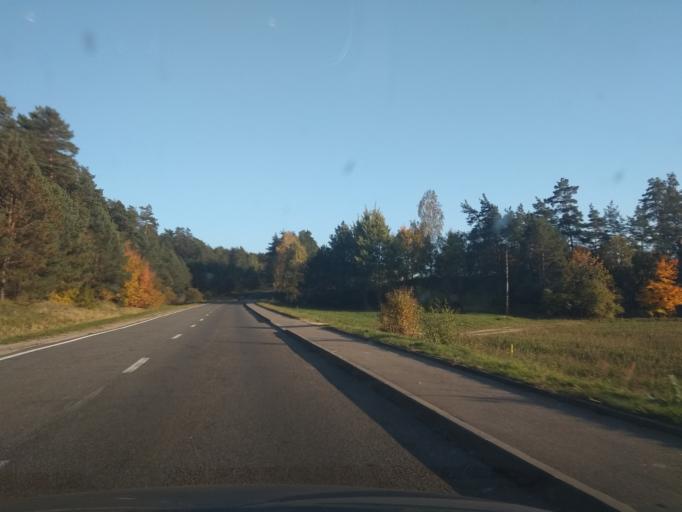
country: BY
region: Grodnenskaya
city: Vawkavysk
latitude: 53.1553
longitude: 24.4925
